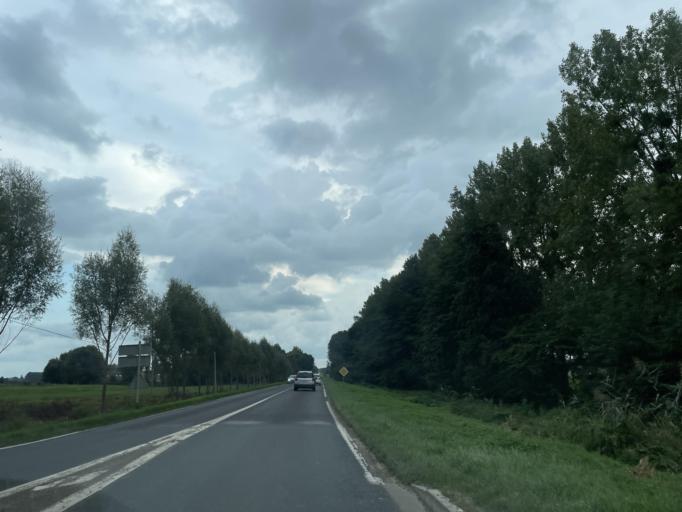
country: FR
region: Haute-Normandie
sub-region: Departement de la Seine-Maritime
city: Gournay-en-Bray
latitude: 49.5053
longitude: 1.6706
